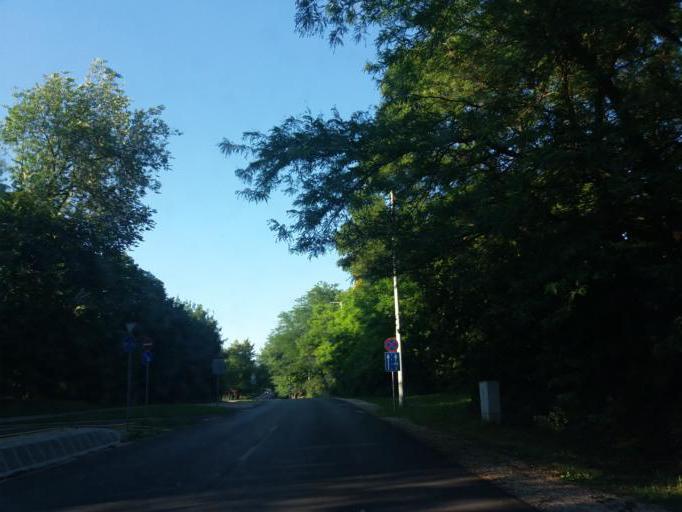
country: HU
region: Fejer
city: Velence
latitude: 47.2313
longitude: 18.6656
